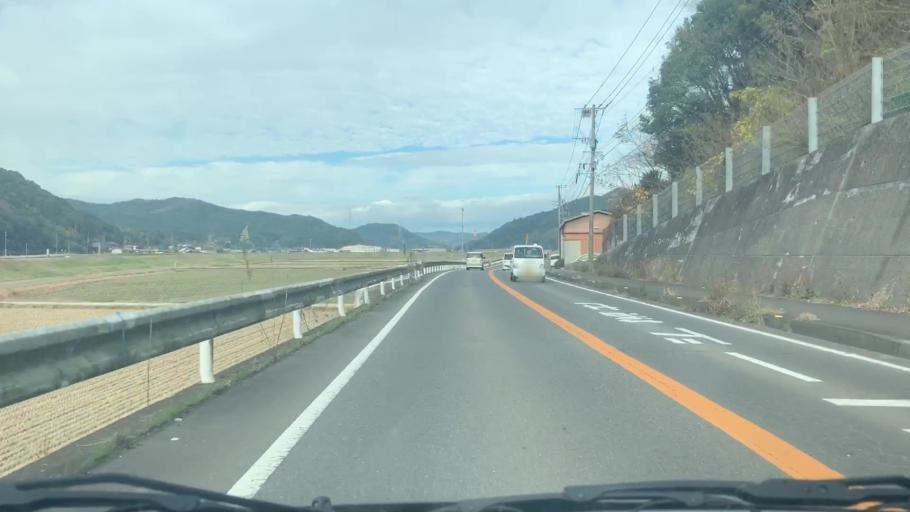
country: JP
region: Saga Prefecture
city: Karatsu
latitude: 33.3651
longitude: 130.0066
